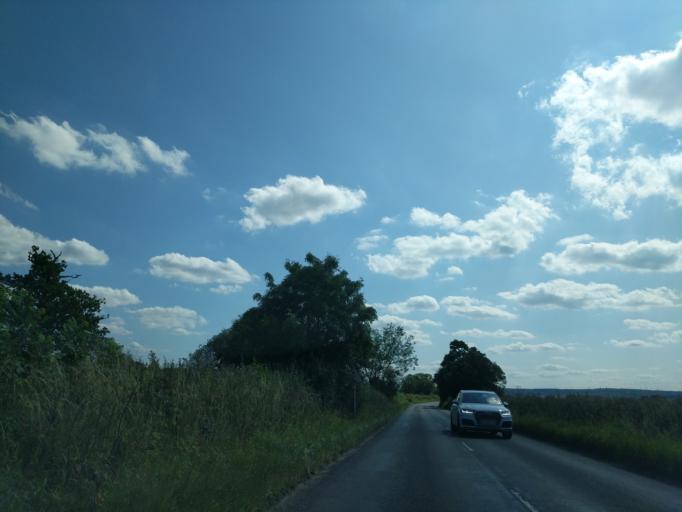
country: GB
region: England
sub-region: Staffordshire
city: Rugeley
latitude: 52.7981
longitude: -1.9314
